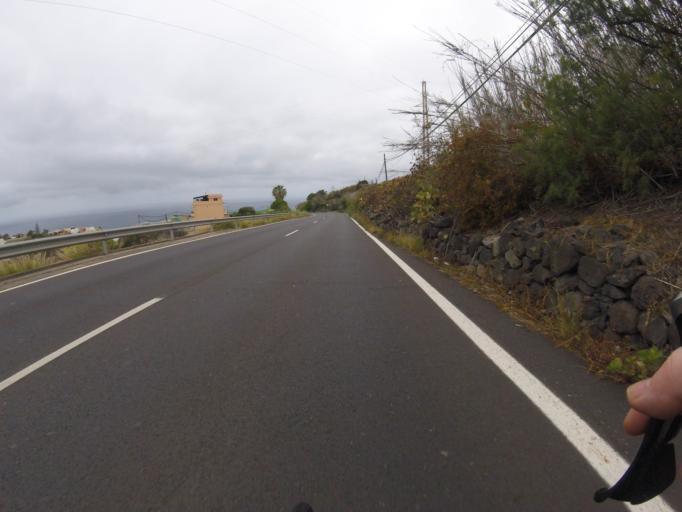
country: ES
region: Canary Islands
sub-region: Provincia de Santa Cruz de Tenerife
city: Tegueste
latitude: 28.5397
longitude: -16.3582
